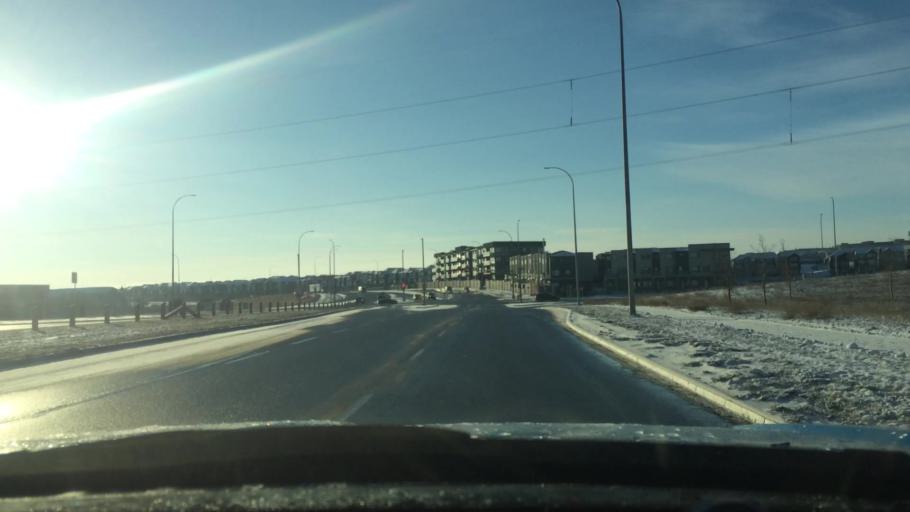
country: CA
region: Alberta
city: Calgary
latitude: 51.1696
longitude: -114.1528
